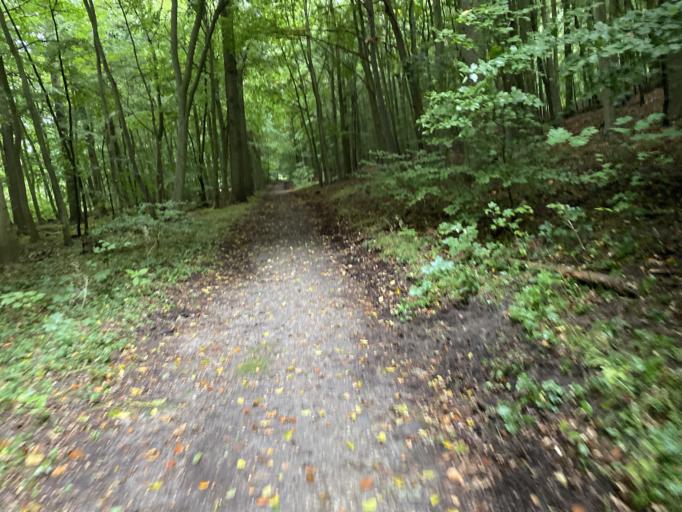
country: DE
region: Mecklenburg-Vorpommern
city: Ostseebad Binz
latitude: 54.4483
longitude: 13.5529
